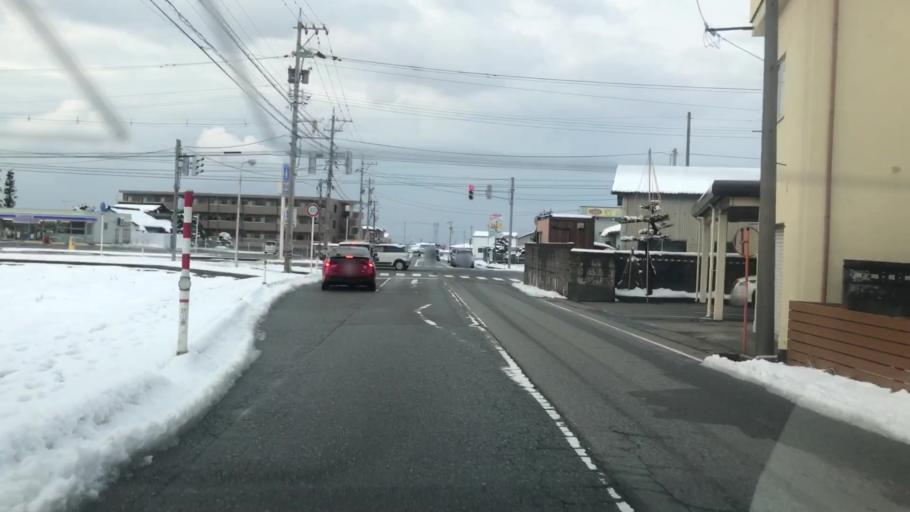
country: JP
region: Toyama
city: Toyama-shi
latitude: 36.6714
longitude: 137.2753
